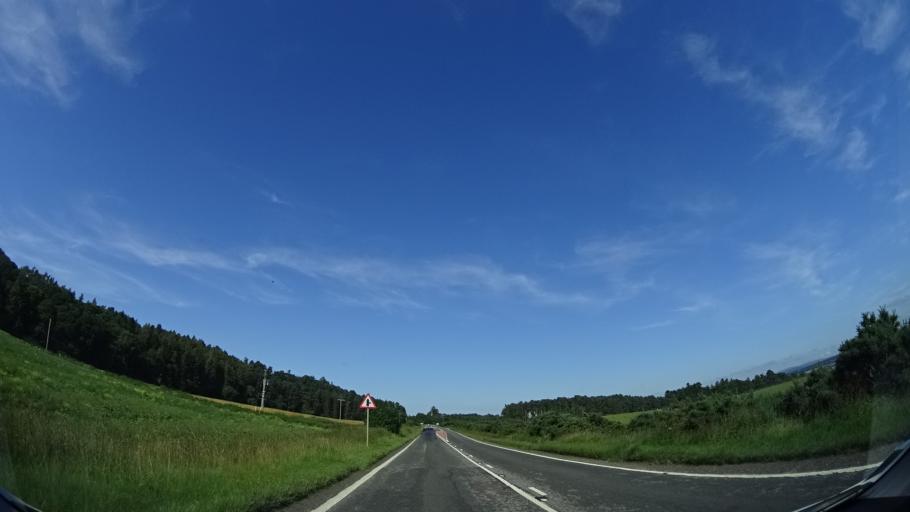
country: GB
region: Scotland
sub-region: Highland
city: Inverness
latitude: 57.4497
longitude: -4.2844
